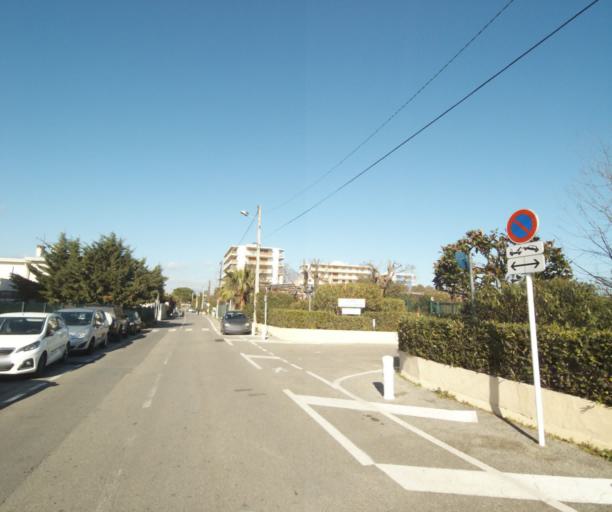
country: FR
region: Provence-Alpes-Cote d'Azur
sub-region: Departement des Alpes-Maritimes
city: Biot
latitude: 43.6074
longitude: 7.1180
